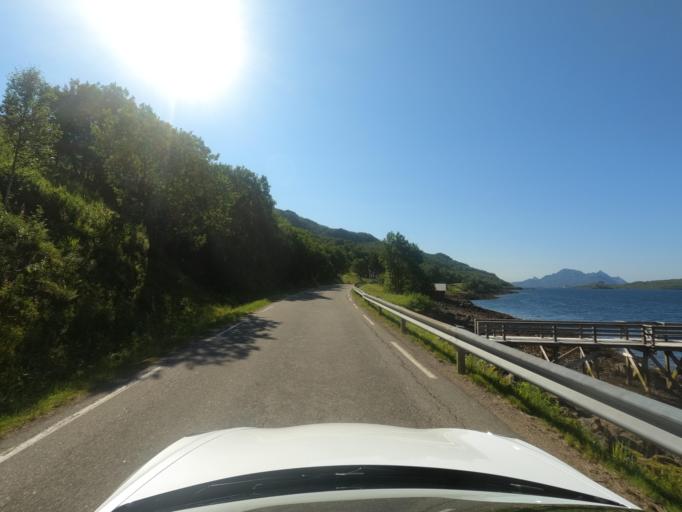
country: NO
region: Nordland
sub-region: Hadsel
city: Stokmarknes
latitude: 68.3828
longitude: 15.0899
